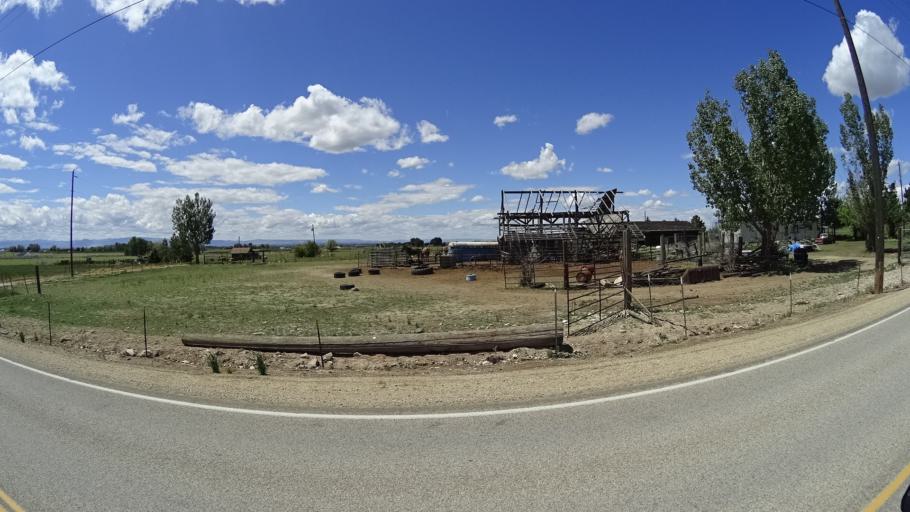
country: US
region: Idaho
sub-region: Ada County
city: Kuna
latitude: 43.5550
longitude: -116.4338
